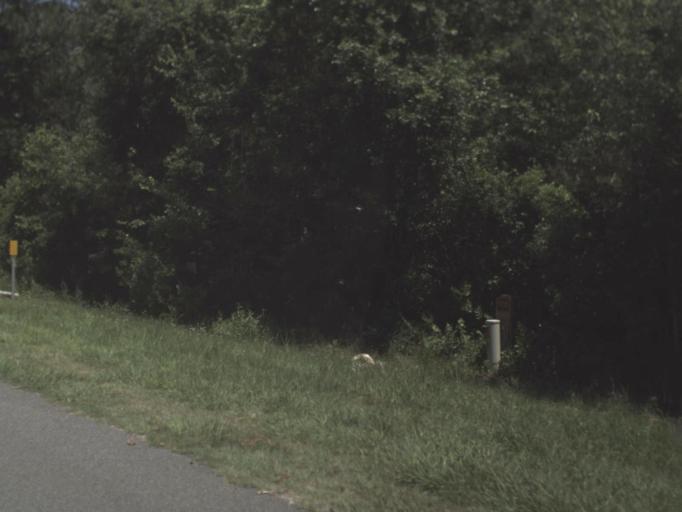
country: US
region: Florida
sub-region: Baker County
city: Macclenny
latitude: 30.2572
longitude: -82.2526
